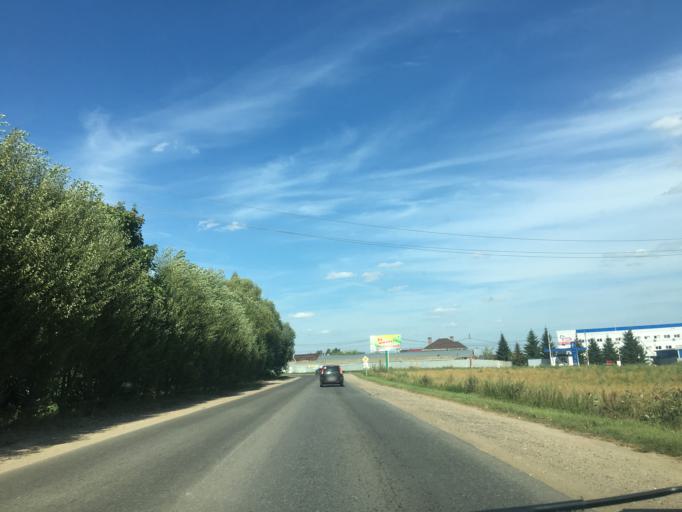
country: RU
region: Moskovskaya
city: Vidnoye
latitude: 55.5092
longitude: 37.6857
